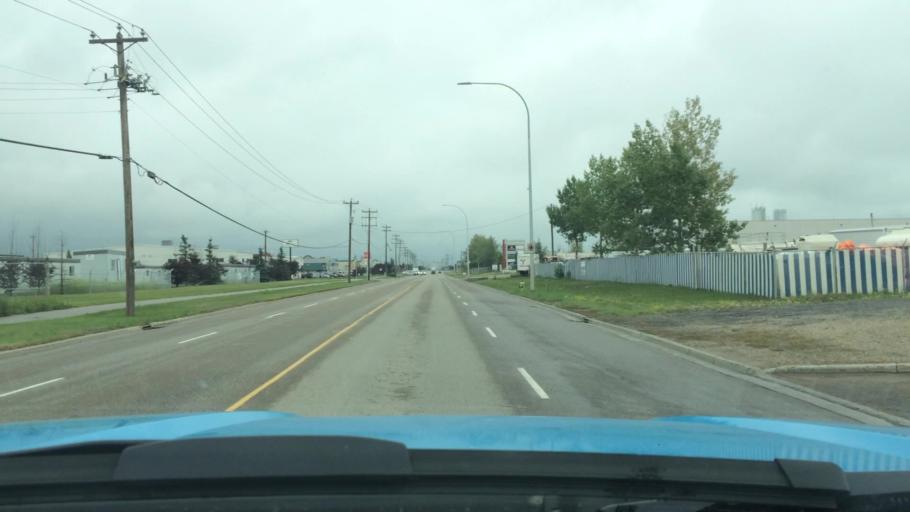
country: CA
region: Alberta
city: Airdrie
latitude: 51.2946
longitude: -113.9899
